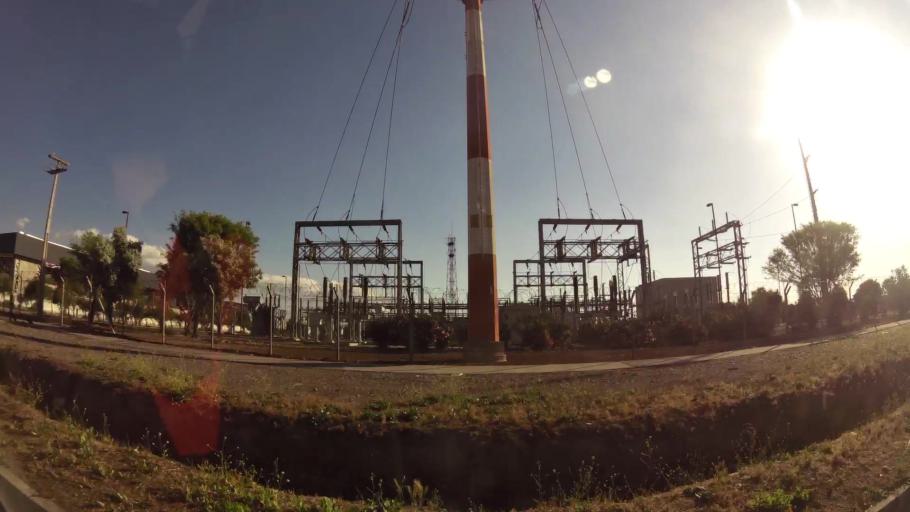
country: CL
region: Santiago Metropolitan
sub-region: Provincia de Maipo
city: San Bernardo
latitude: -33.5400
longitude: -70.7646
